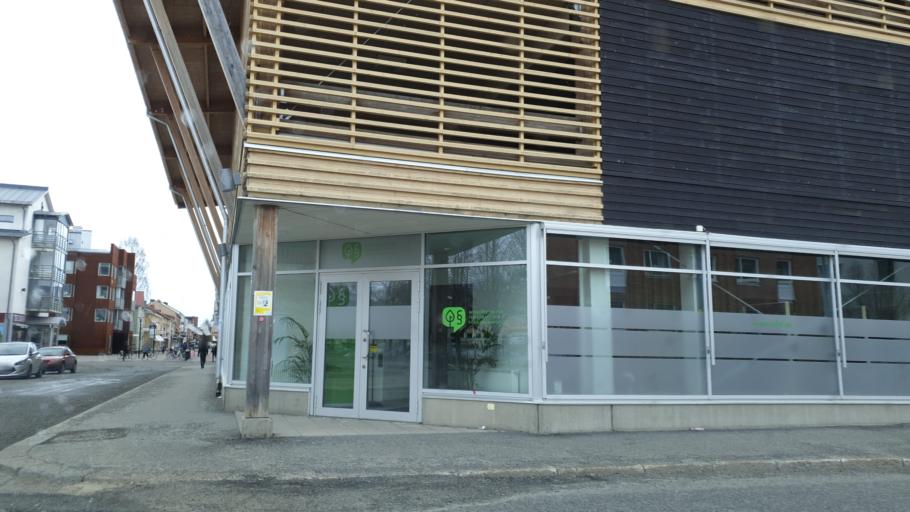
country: SE
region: Vaesterbotten
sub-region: Skelleftea Kommun
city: Skelleftea
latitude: 64.7511
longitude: 20.9449
